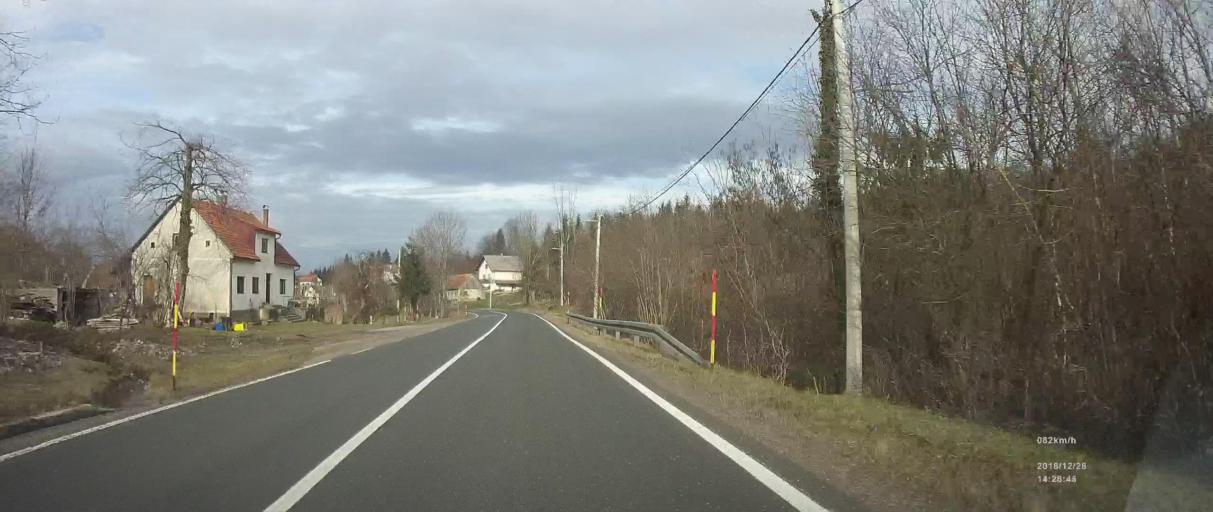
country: HR
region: Primorsko-Goranska
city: Vrbovsko
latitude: 45.4132
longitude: 15.1166
